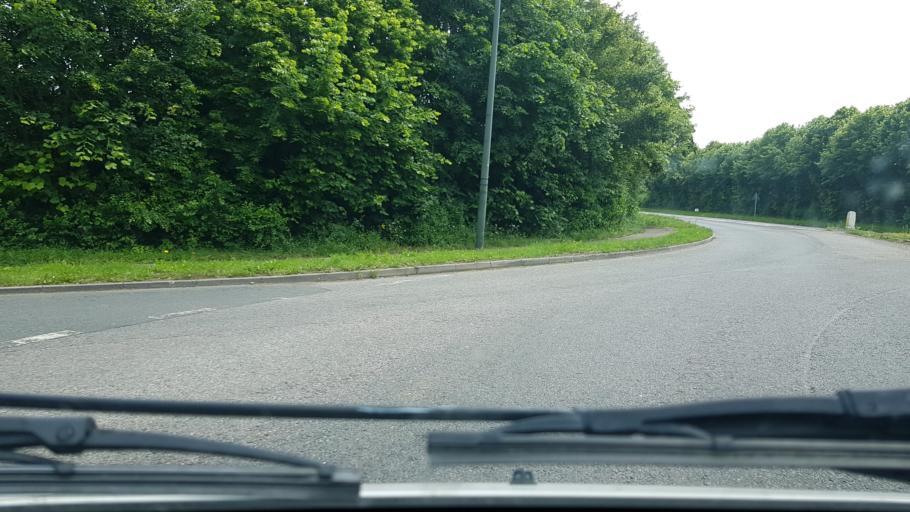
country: GB
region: England
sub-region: Worcestershire
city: Broadway
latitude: 52.0473
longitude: -1.8570
